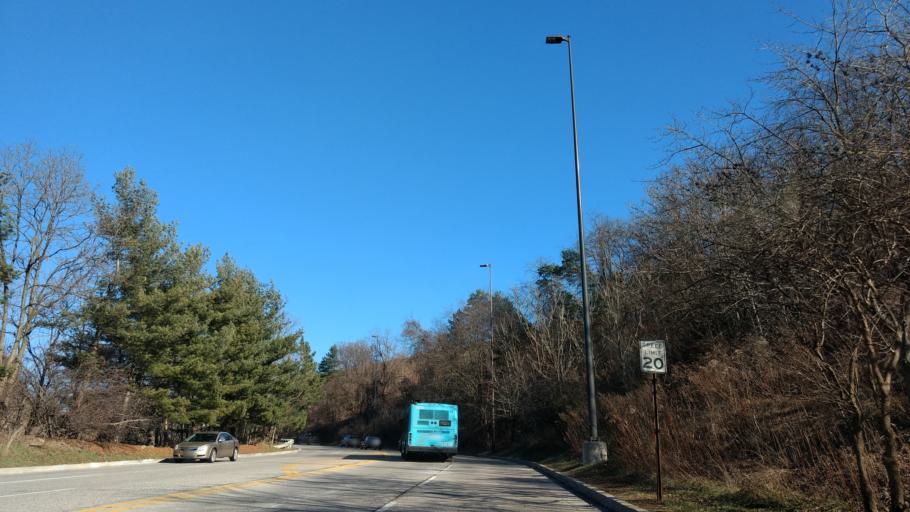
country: US
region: Pennsylvania
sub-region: Allegheny County
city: West View
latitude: 40.5424
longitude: -80.0120
